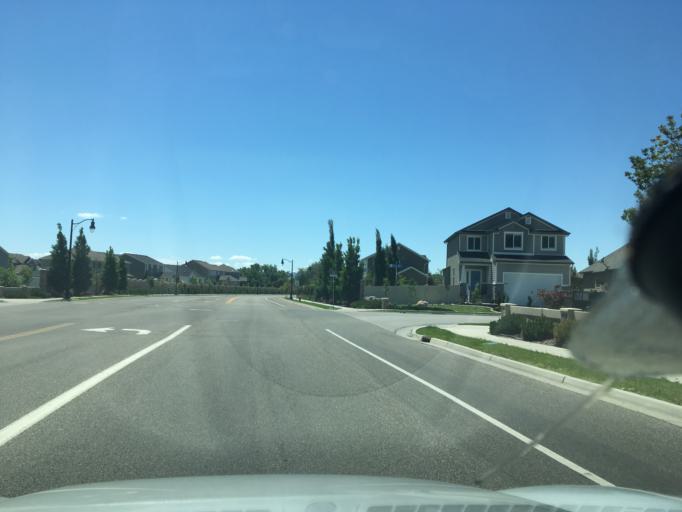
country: US
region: Utah
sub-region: Davis County
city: Layton
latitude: 41.0502
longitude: -111.9784
